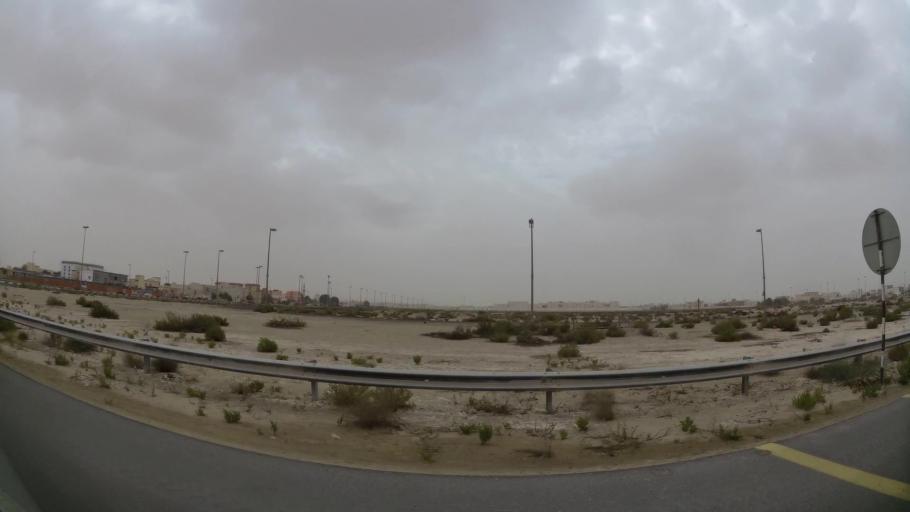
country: AE
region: Abu Dhabi
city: Abu Dhabi
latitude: 24.4030
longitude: 54.7335
